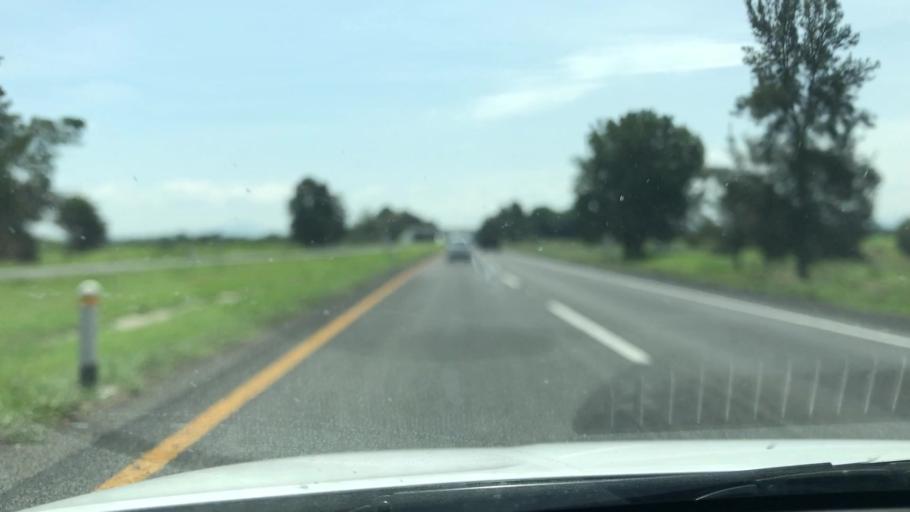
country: MX
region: Jalisco
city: La Barca
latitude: 20.3220
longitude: -102.5259
